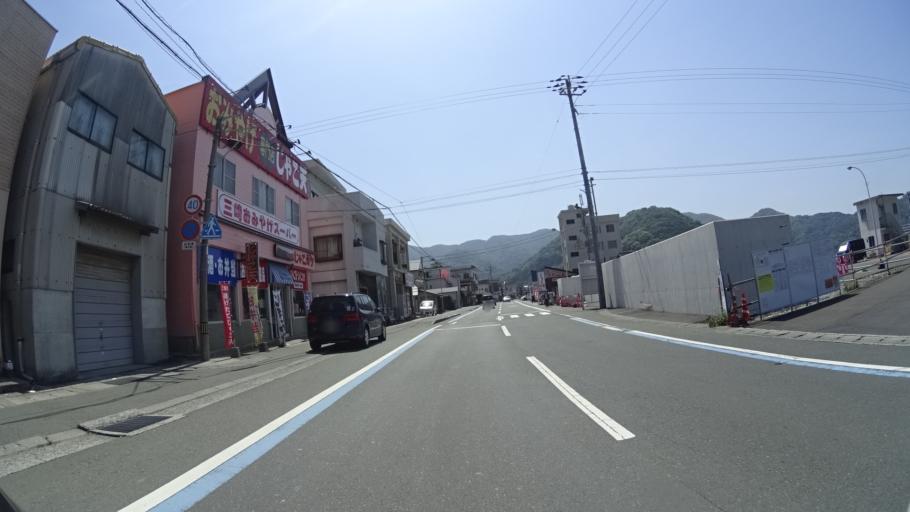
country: JP
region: Ehime
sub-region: Nishiuwa-gun
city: Ikata-cho
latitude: 33.3914
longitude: 132.1185
